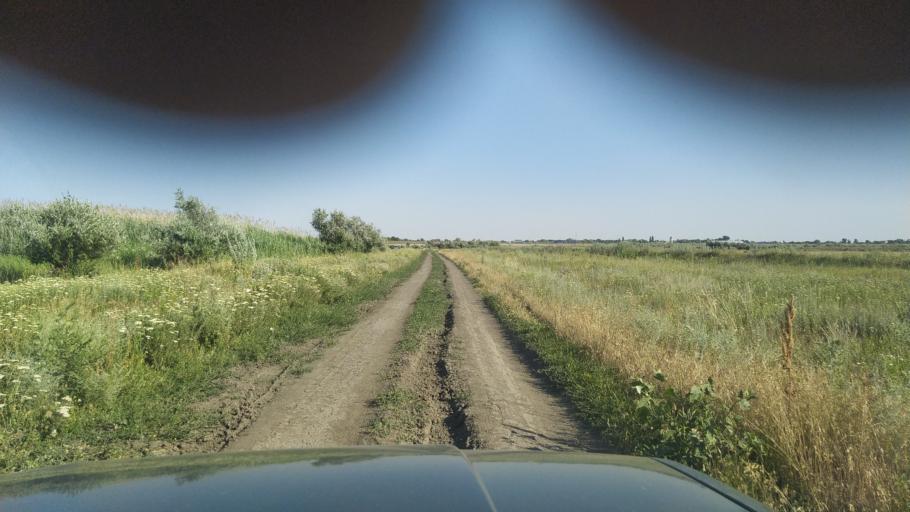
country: RU
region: Rostov
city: Kuleshovka
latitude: 47.1232
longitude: 39.6479
